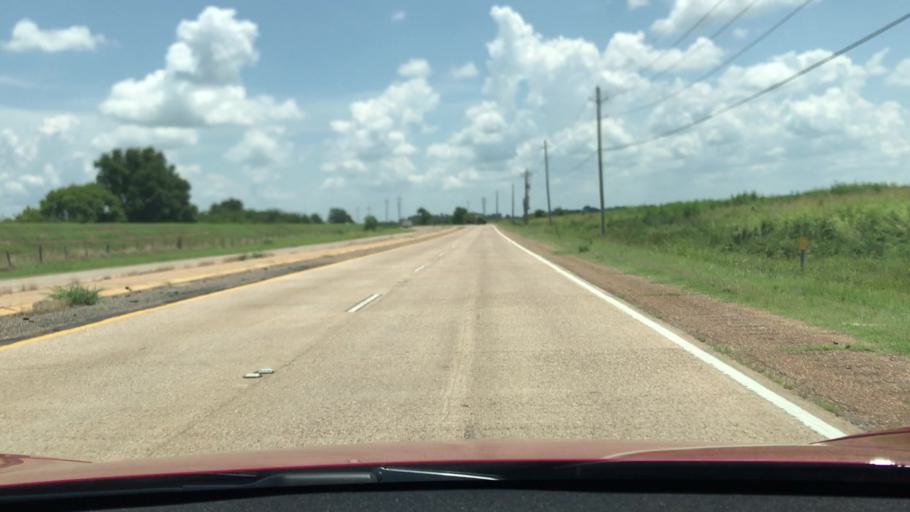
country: US
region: Louisiana
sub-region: Bossier Parish
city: Bossier City
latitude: 32.3924
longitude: -93.6858
